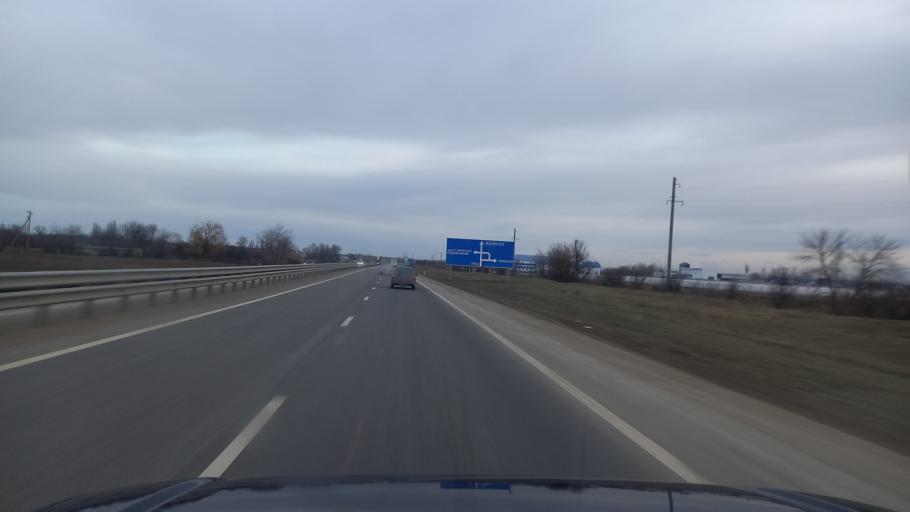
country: RU
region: Adygeya
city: Khanskaya
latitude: 44.6917
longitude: 39.9731
